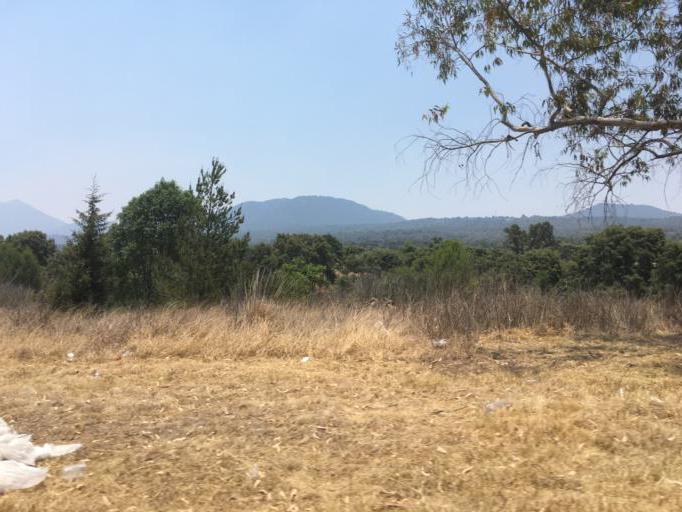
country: MX
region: Michoacan
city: Quiroga
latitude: 19.6392
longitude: -101.4840
